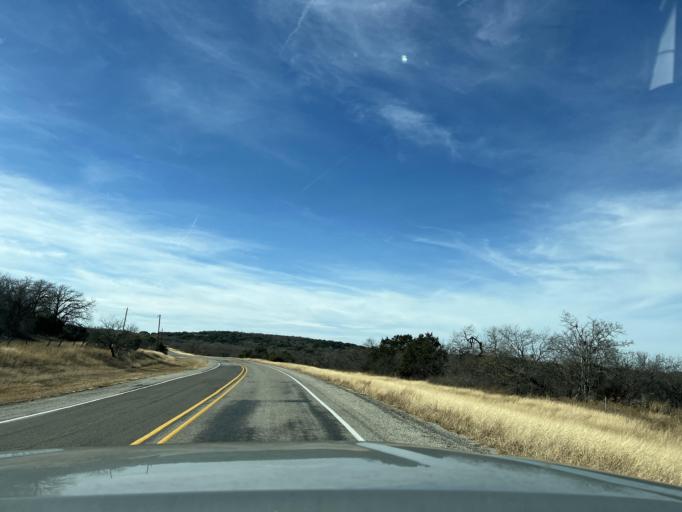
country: US
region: Texas
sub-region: Eastland County
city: Cisco
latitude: 32.4643
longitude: -99.0187
